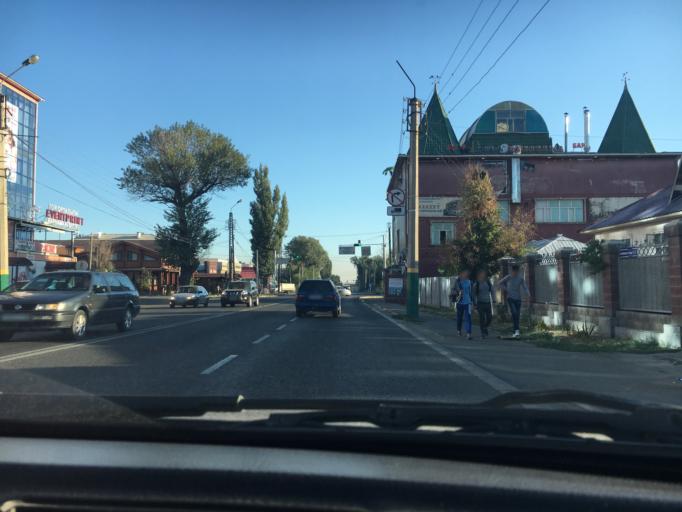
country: KZ
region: Zhambyl
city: Taraz
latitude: 42.8942
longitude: 71.3606
